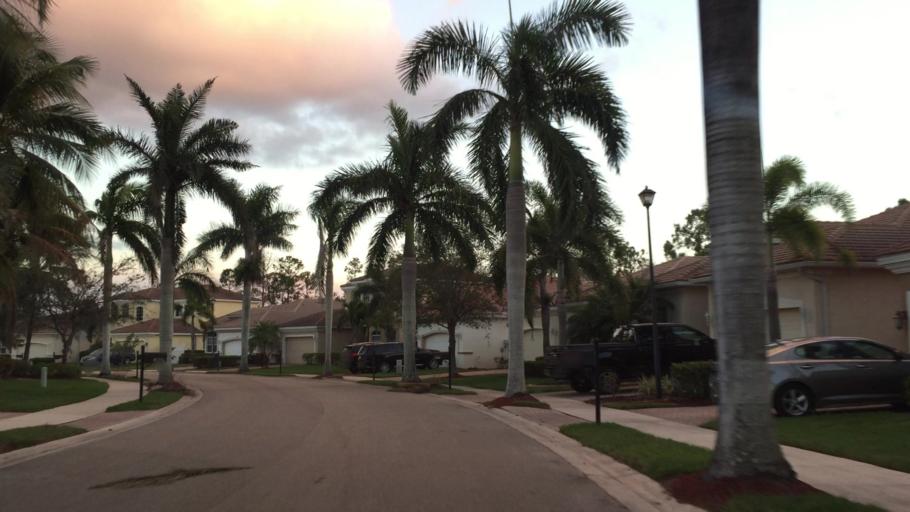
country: US
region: Florida
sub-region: Lee County
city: Gateway
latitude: 26.6229
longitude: -81.7623
